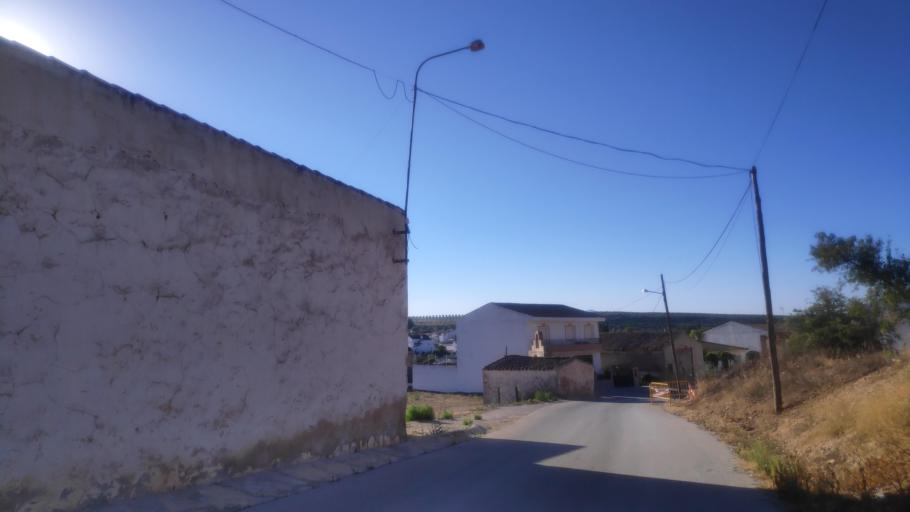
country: ES
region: Andalusia
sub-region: Provincia de Jaen
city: Hinojares
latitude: 37.6737
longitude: -2.9737
